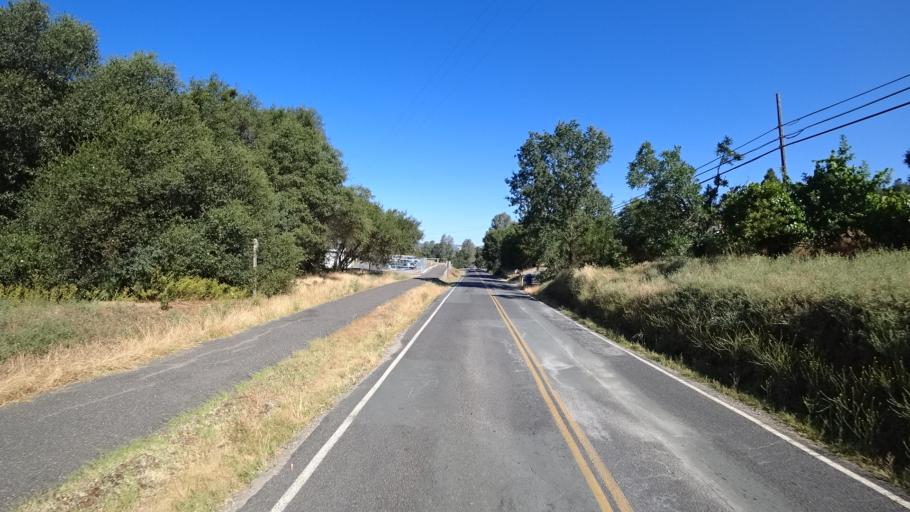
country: US
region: California
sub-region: Calaveras County
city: San Andreas
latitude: 38.2019
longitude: -120.6787
